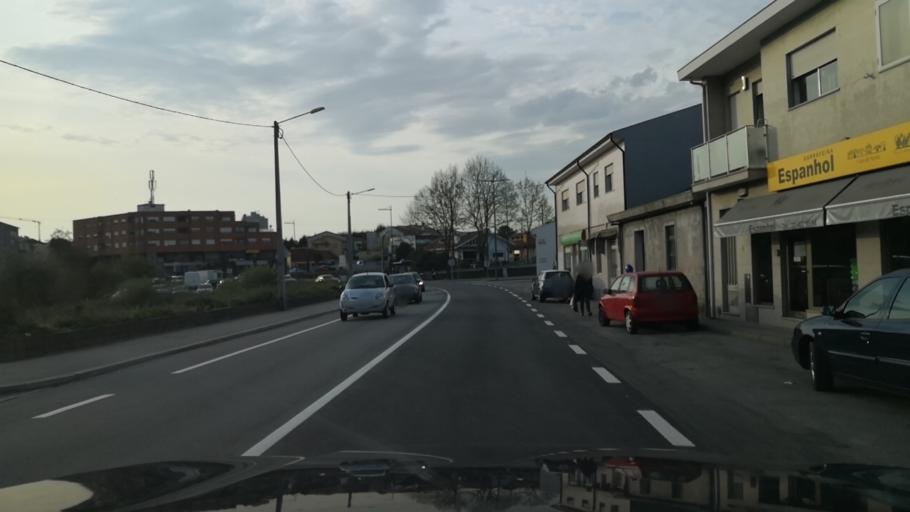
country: PT
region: Porto
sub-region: Valongo
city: Valongo
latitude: 41.1871
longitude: -8.4886
